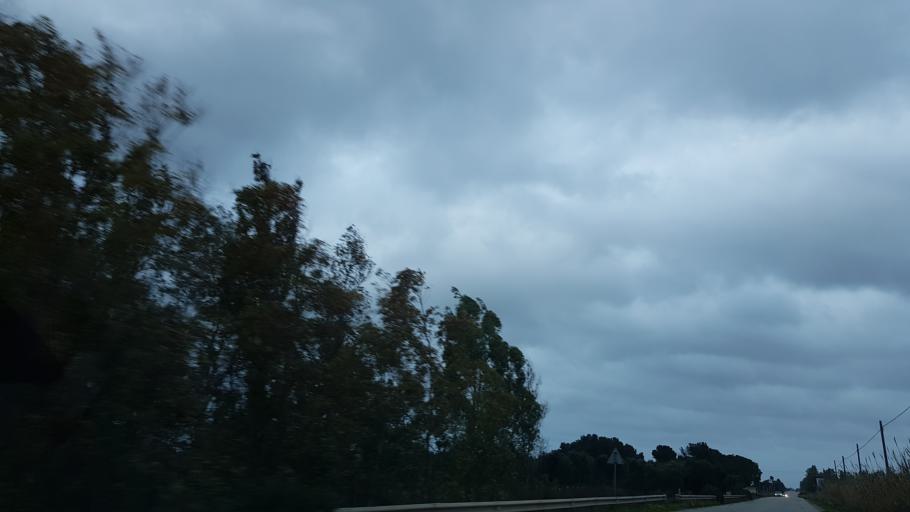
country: IT
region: Apulia
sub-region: Provincia di Brindisi
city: Mesagne
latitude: 40.6508
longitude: 17.8250
